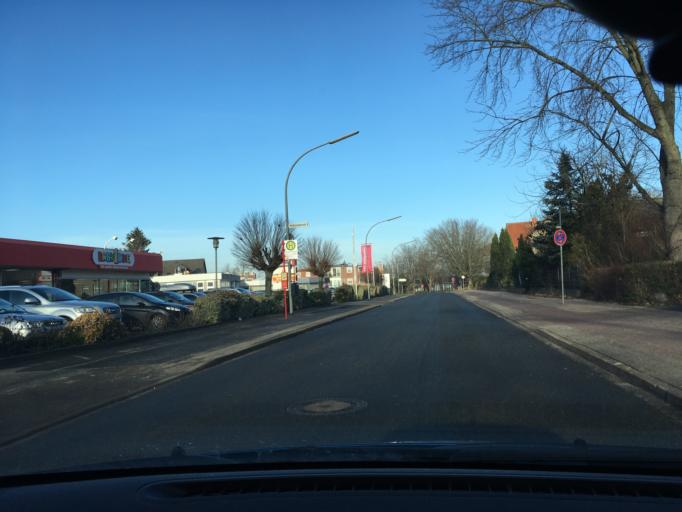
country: DE
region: Lower Saxony
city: Lueneburg
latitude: 53.2458
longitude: 10.4222
